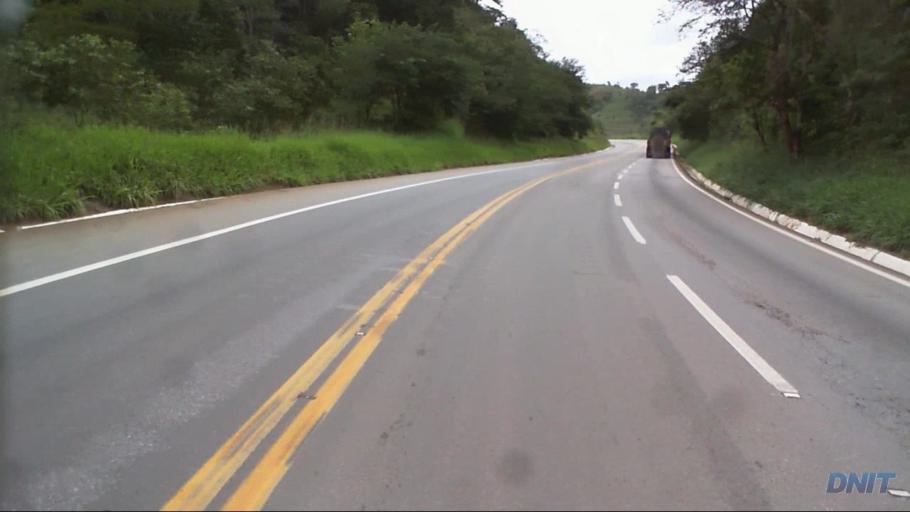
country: BR
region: Minas Gerais
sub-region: Barao De Cocais
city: Barao de Cocais
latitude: -19.8351
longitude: -43.3640
